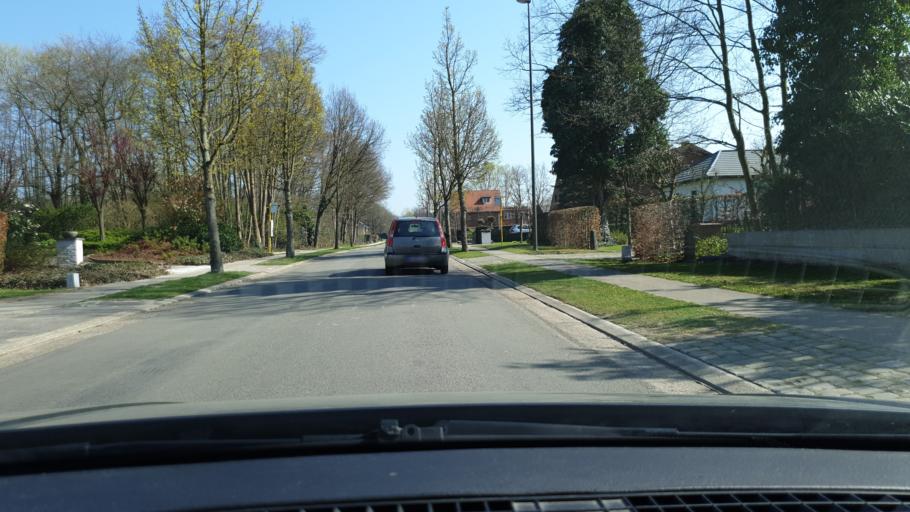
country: BE
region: Flanders
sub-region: Provincie Limburg
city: Zonhoven
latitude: 50.9596
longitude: 5.3630
